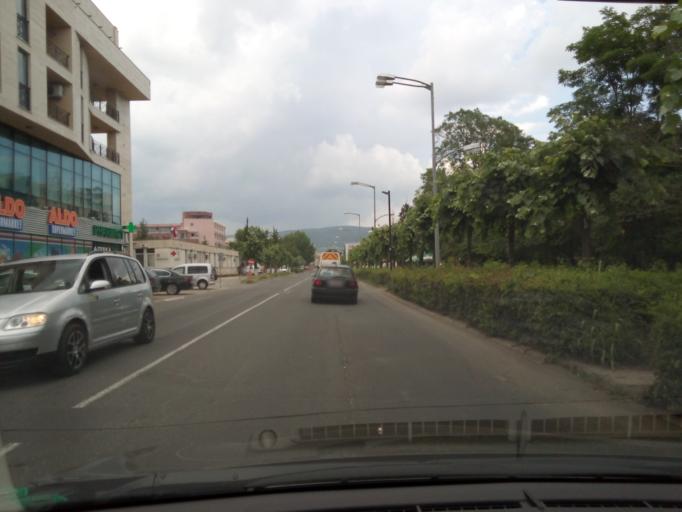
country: BG
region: Burgas
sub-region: Obshtina Nesebur
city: Nesebar
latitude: 42.6977
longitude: 27.7118
